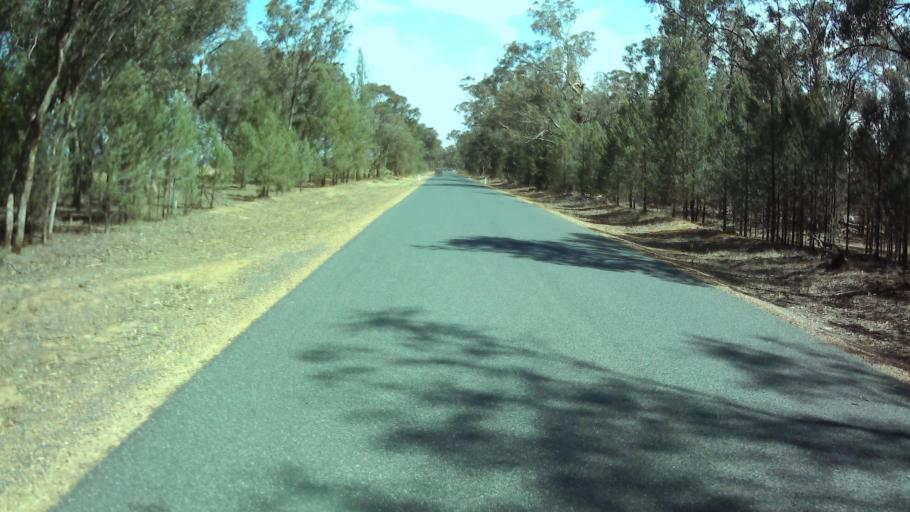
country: AU
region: New South Wales
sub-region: Weddin
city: Grenfell
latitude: -34.0331
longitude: 148.1339
